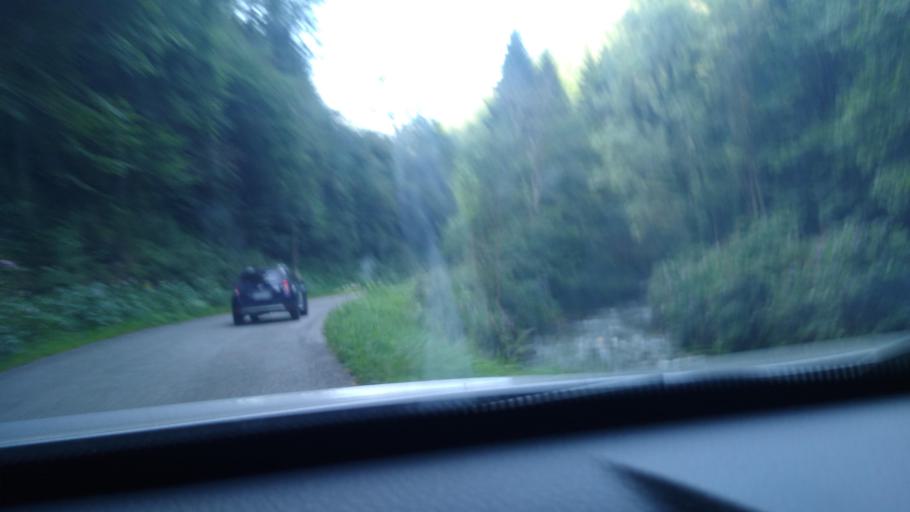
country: FR
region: Midi-Pyrenees
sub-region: Departement de l'Ariege
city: Saint-Girons
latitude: 42.8029
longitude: 1.1941
